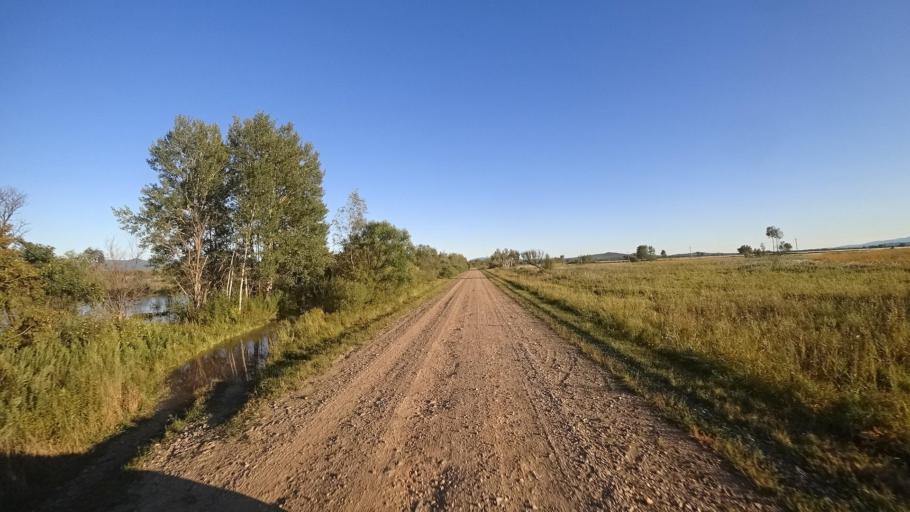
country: RU
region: Primorskiy
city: Kirovskiy
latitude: 44.8068
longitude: 133.6179
